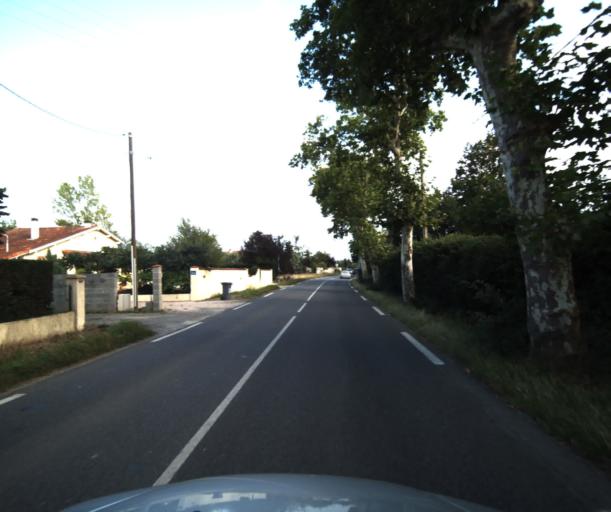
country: FR
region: Midi-Pyrenees
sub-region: Departement de la Haute-Garonne
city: Muret
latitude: 43.4457
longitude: 1.3381
